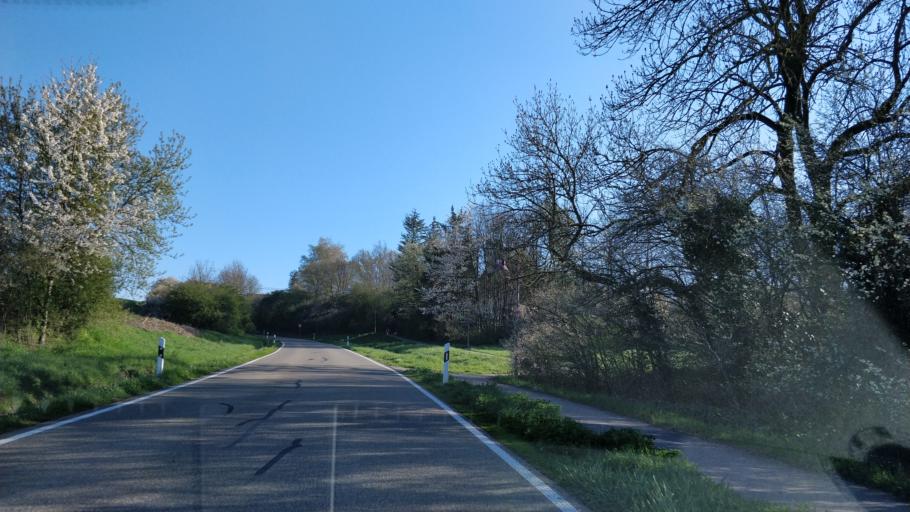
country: DE
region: Baden-Wuerttemberg
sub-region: Regierungsbezirk Stuttgart
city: Michelbach an der Bilz
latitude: 49.0543
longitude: 9.7242
